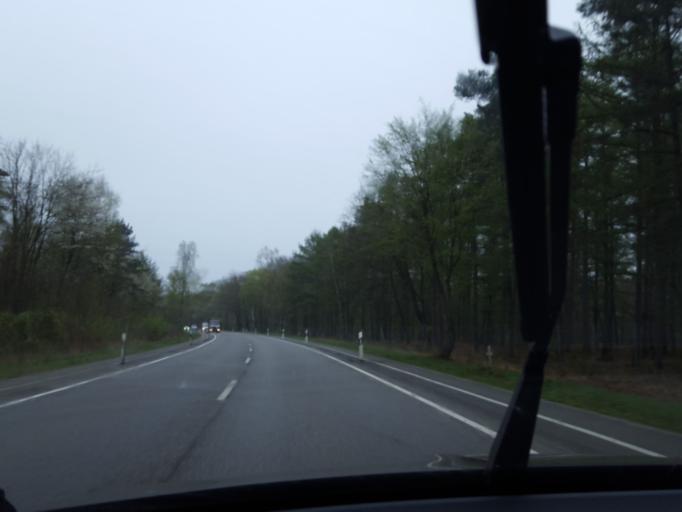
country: DE
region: North Rhine-Westphalia
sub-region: Regierungsbezirk Dusseldorf
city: Schermbeck
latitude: 51.7207
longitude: 6.9211
